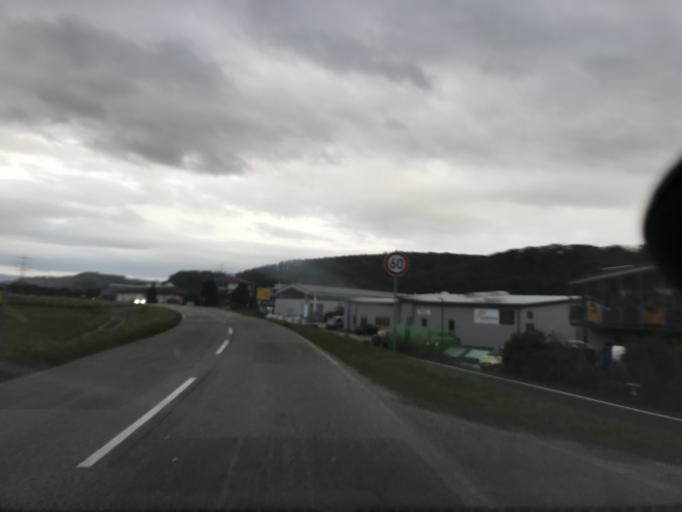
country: DE
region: Baden-Wuerttemberg
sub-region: Freiburg Region
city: Steinen
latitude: 47.6426
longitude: 7.7024
